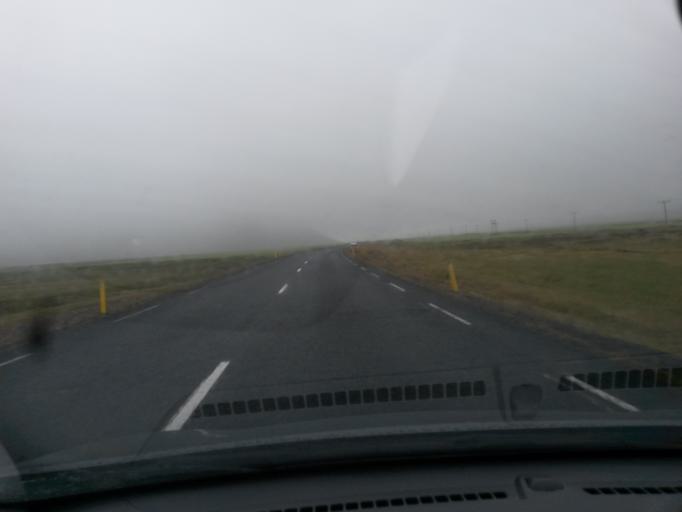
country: IS
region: South
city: Vestmannaeyjar
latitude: 63.4627
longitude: -19.2323
